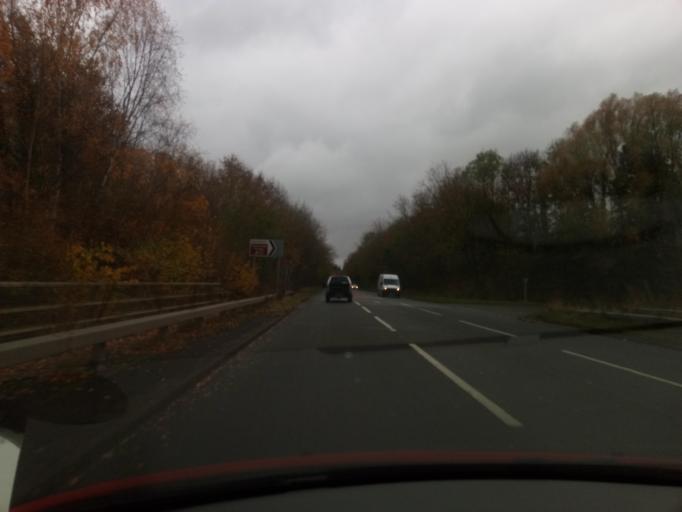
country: GB
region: England
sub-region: County Durham
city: High Etherley
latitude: 54.6708
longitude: -1.7759
